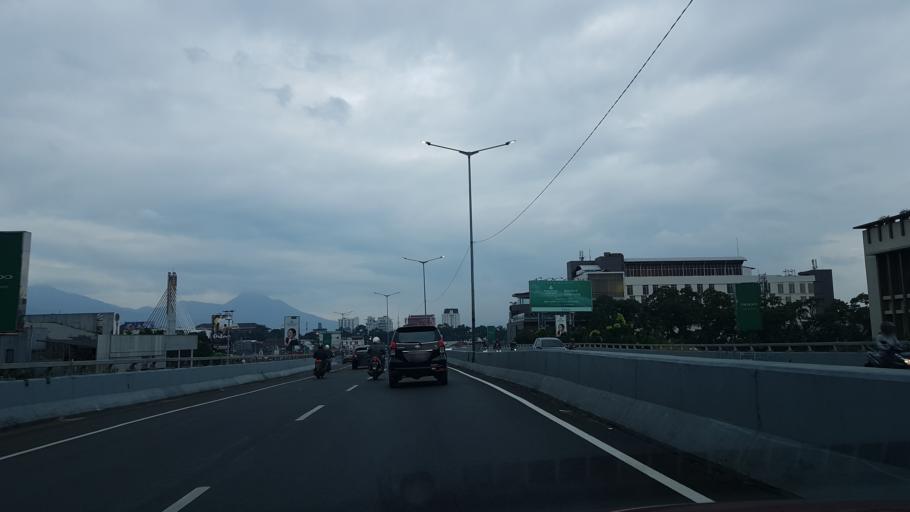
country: ID
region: West Java
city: Bandung
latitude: -6.9003
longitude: 107.6028
